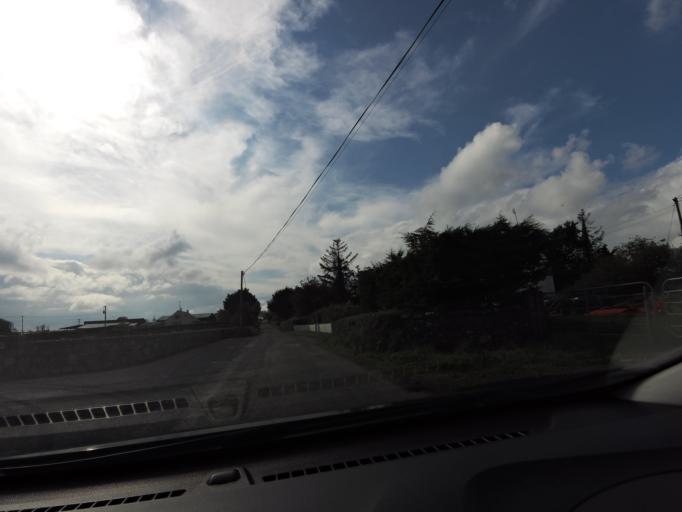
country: IE
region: Connaught
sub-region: County Galway
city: Athenry
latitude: 53.3084
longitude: -8.8091
